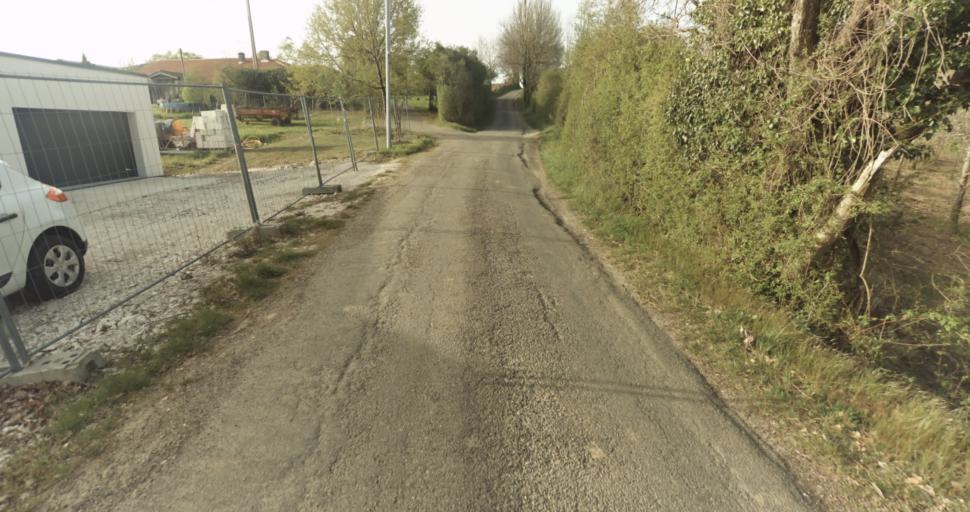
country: FR
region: Midi-Pyrenees
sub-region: Departement du Tarn-et-Garonne
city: Moissac
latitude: 44.1263
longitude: 1.1117
